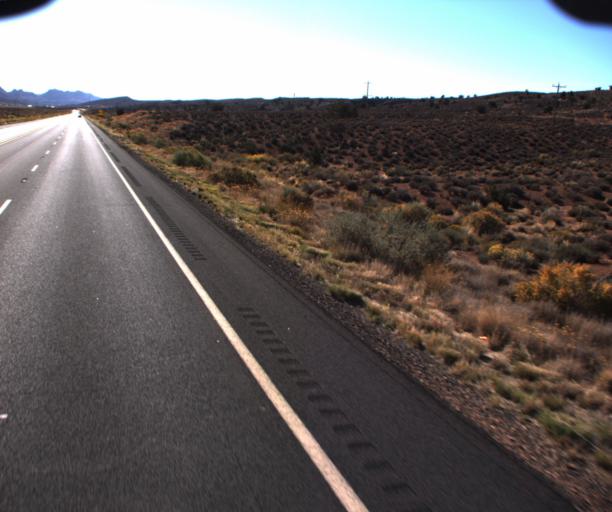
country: US
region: Arizona
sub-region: Coconino County
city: Tuba City
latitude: 36.3303
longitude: -111.4891
